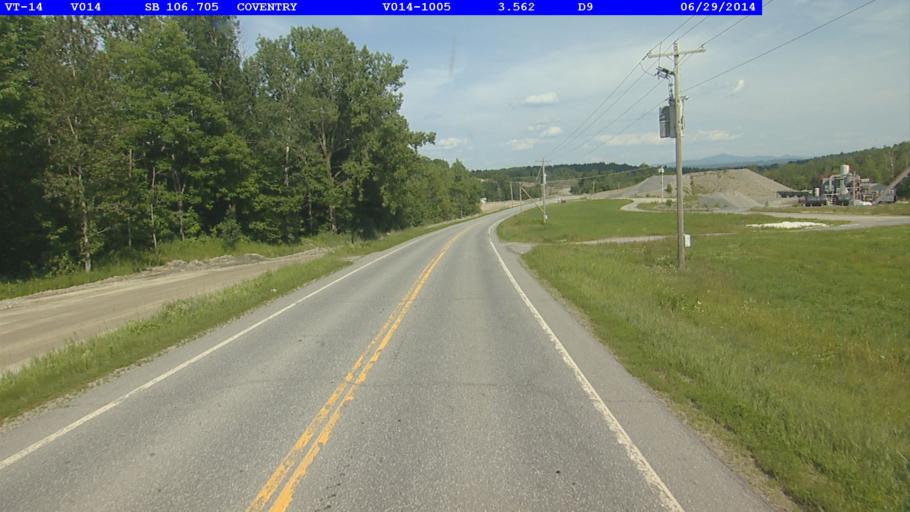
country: US
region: Vermont
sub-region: Orleans County
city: Newport
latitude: 44.9112
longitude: -72.2677
